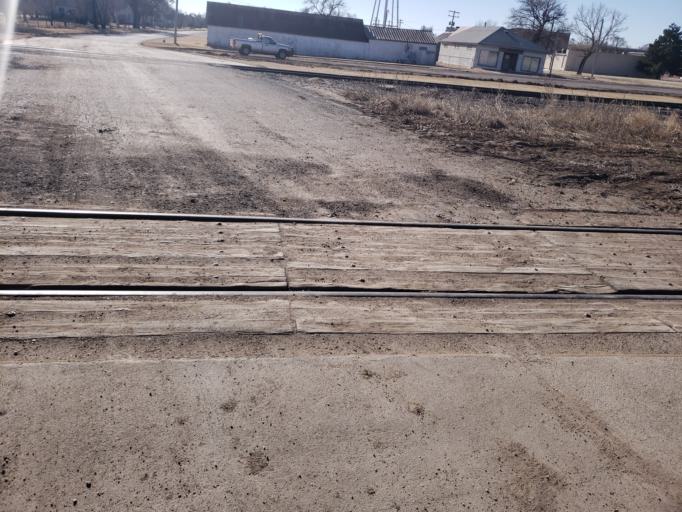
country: US
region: Kansas
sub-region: Ness County
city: Ness City
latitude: 38.4457
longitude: -99.6906
